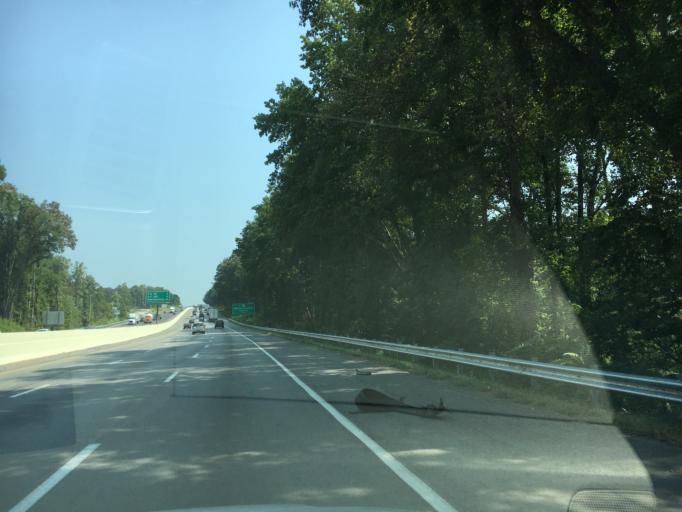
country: US
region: South Carolina
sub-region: Spartanburg County
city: Wellford
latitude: 34.9239
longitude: -82.0919
